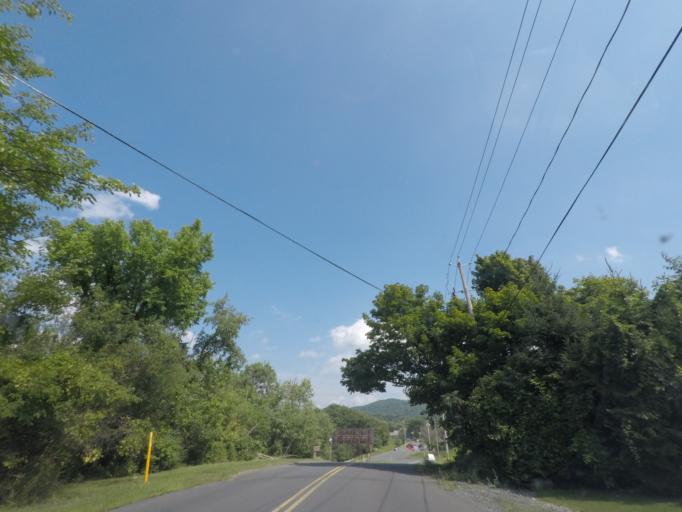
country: US
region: New York
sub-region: Saratoga County
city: Waterford
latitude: 42.7848
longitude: -73.6572
